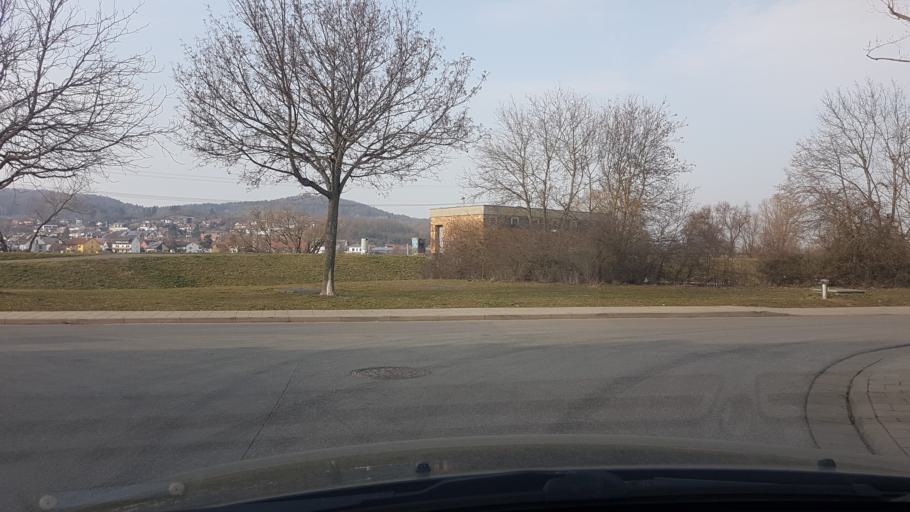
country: DE
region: Bavaria
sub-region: Upper Franconia
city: Hallstadt
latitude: 49.9264
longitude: 10.8666
